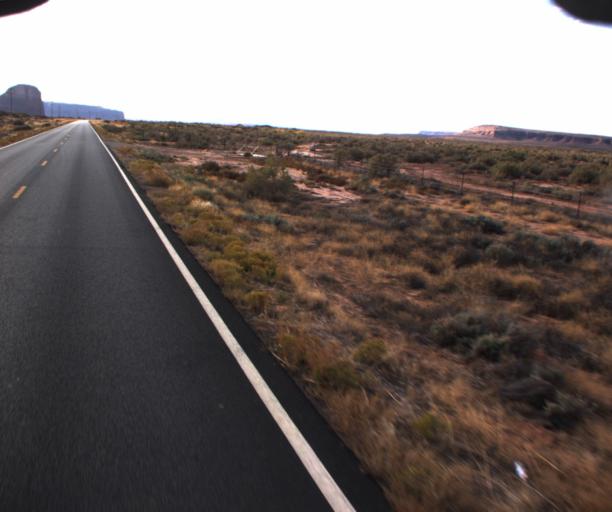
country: US
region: Arizona
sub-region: Apache County
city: Many Farms
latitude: 36.6870
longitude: -109.6073
